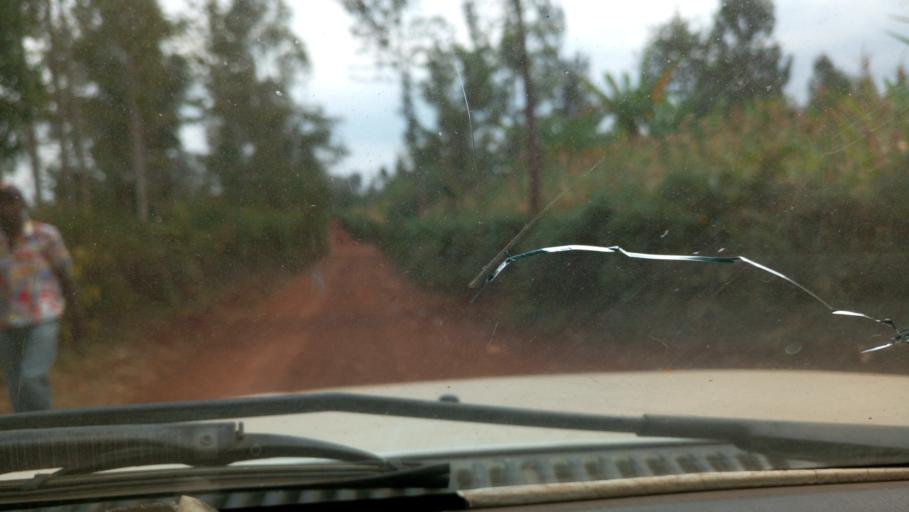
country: KE
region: Murang'a District
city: Maragua
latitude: -0.8644
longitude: 37.0566
